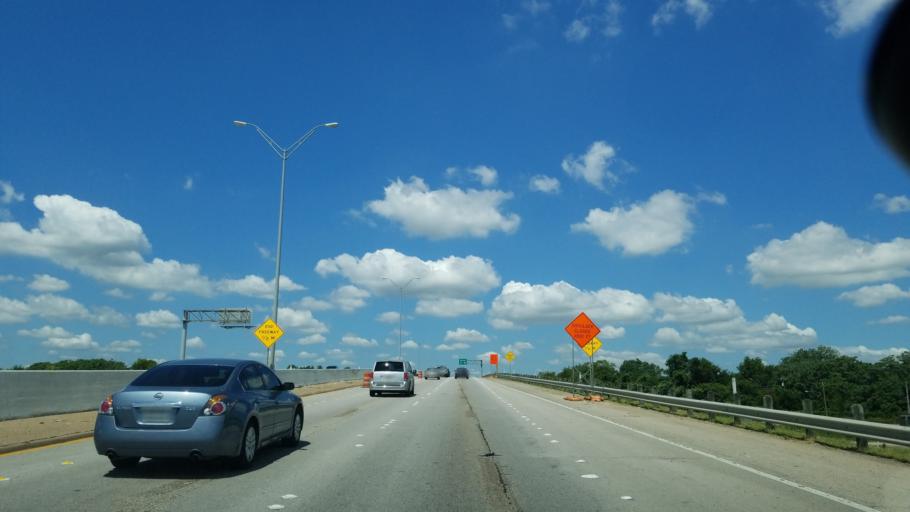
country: US
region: Texas
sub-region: Dallas County
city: Dallas
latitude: 32.7473
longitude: -96.7484
